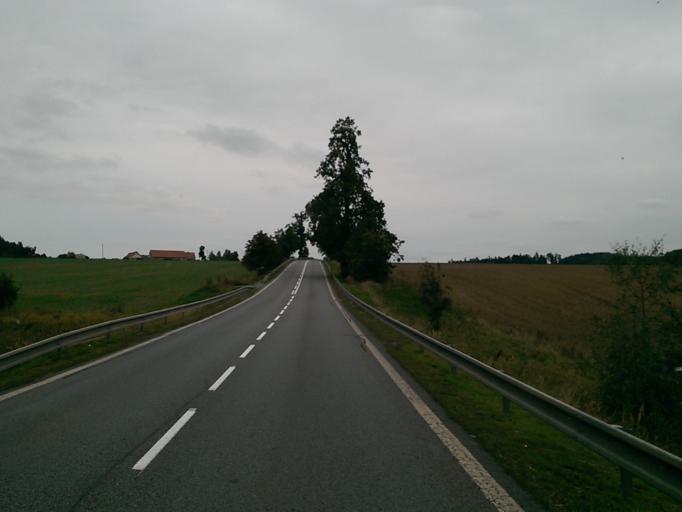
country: CZ
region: Vysocina
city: Zeletava
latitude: 49.1188
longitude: 15.7051
